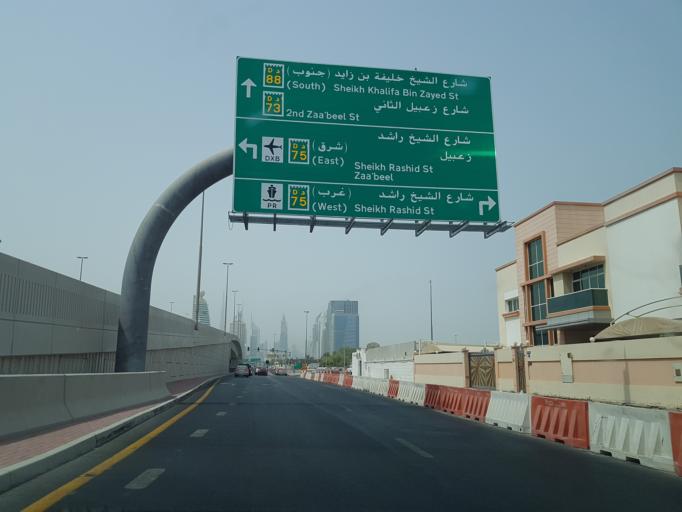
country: AE
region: Ash Shariqah
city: Sharjah
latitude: 25.2413
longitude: 55.2961
